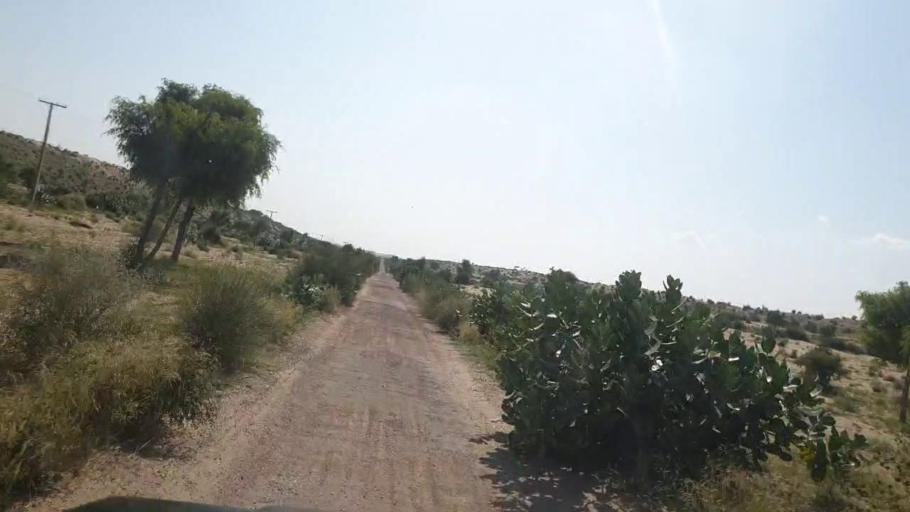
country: PK
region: Sindh
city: Chor
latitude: 25.5629
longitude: 70.2295
